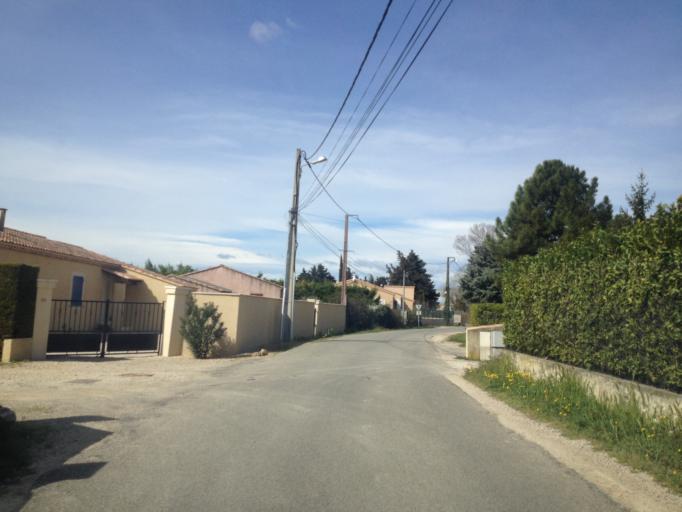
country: FR
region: Provence-Alpes-Cote d'Azur
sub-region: Departement du Vaucluse
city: Camaret-sur-Aigues
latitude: 44.1680
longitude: 4.8635
